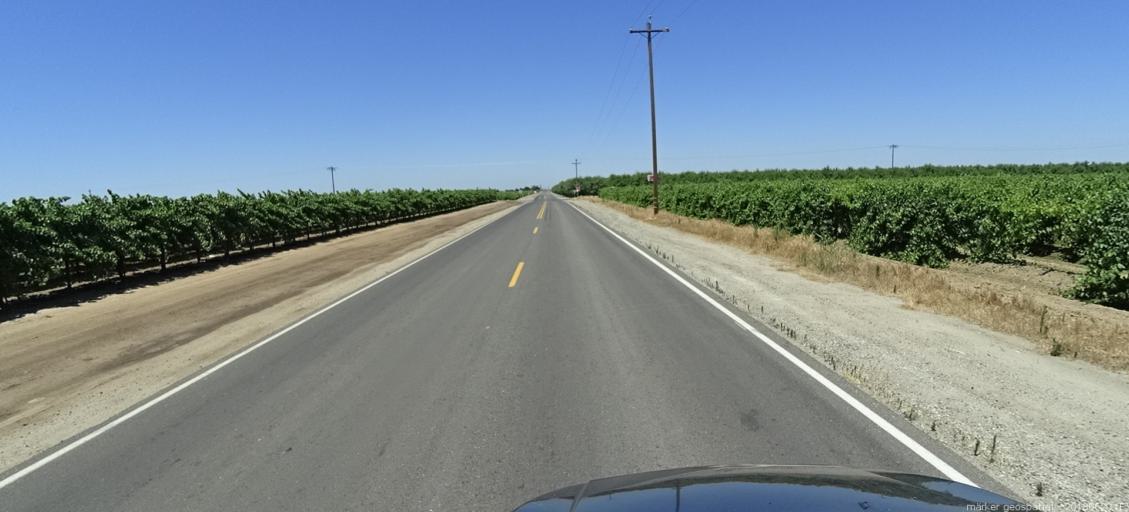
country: US
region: California
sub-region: Madera County
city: Parkwood
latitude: 36.8804
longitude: -119.9999
